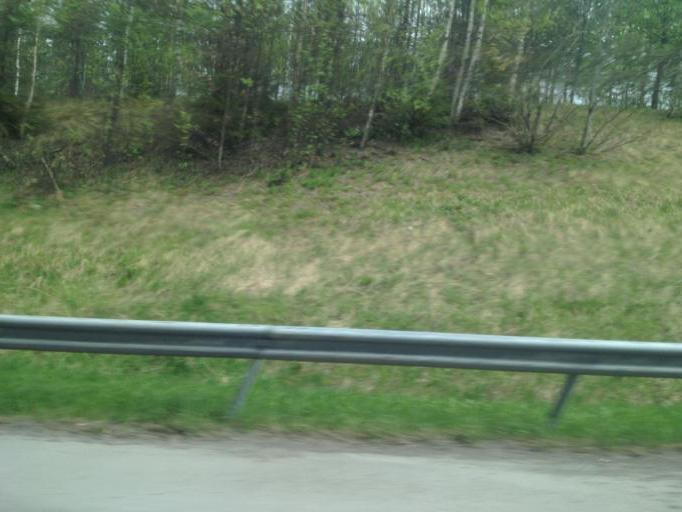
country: FI
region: Uusimaa
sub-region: Helsinki
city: Hyvinge
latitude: 60.5888
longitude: 24.7982
